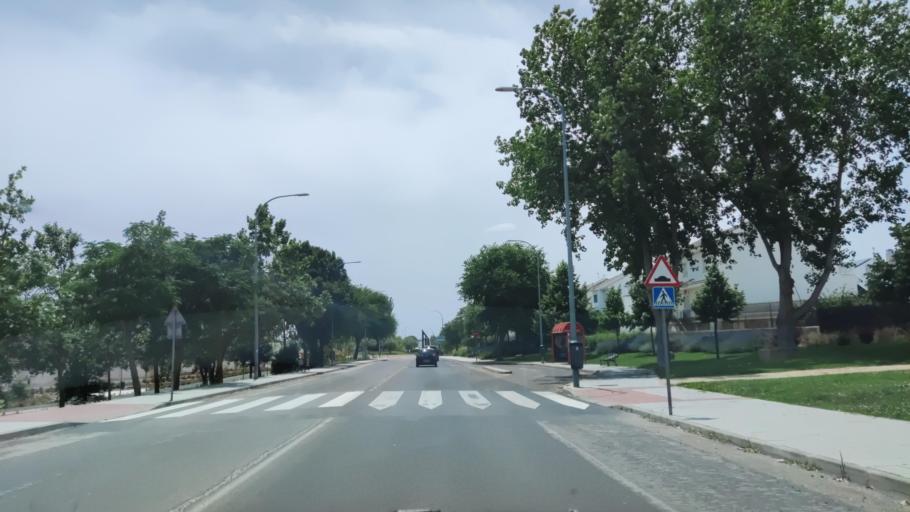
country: ES
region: Madrid
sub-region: Provincia de Madrid
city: Navalcarnero
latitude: 40.2821
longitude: -4.0243
